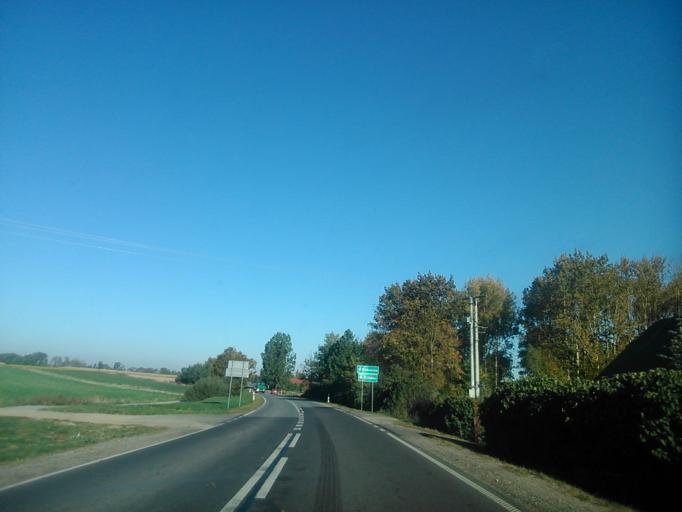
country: PL
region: Kujawsko-Pomorskie
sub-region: Powiat wabrzeski
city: Debowa Laka
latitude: 53.2165
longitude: 19.0312
